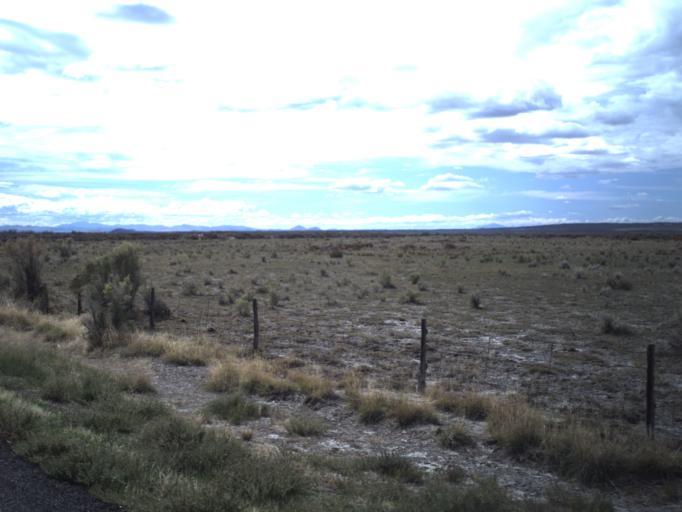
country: US
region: Utah
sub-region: Millard County
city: Fillmore
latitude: 39.1151
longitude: -112.4095
